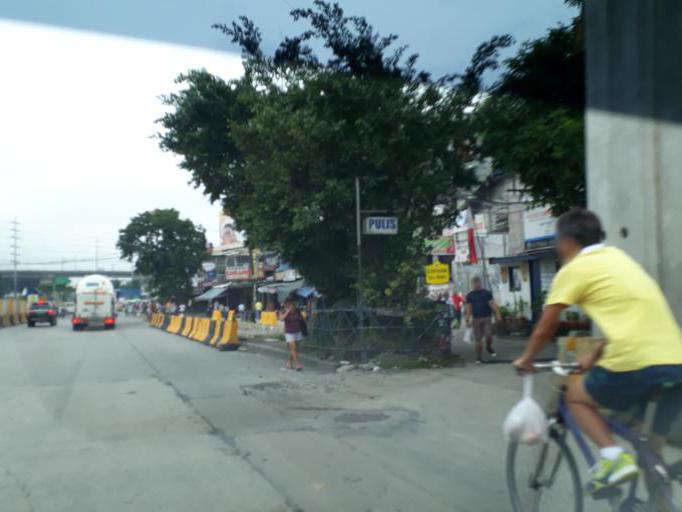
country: PH
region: Calabarzon
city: Del Monte
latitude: 14.6547
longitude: 120.9989
